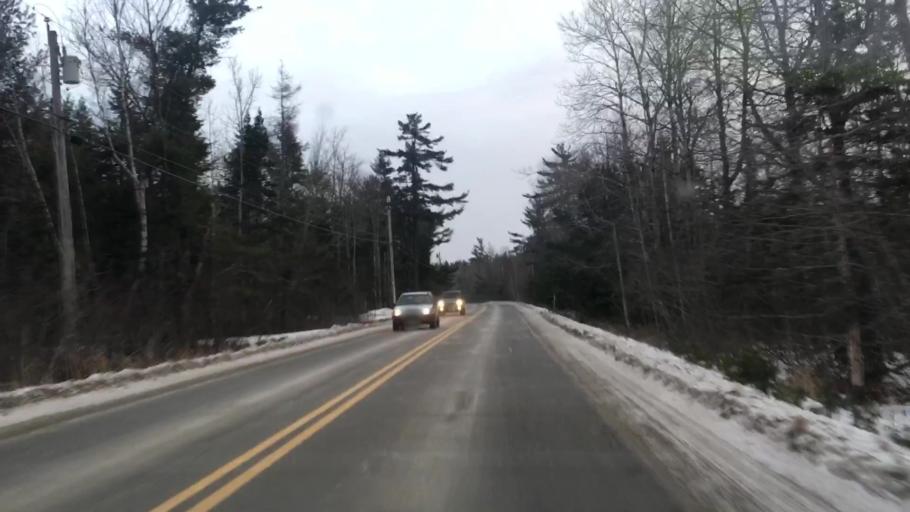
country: US
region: Maine
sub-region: Hancock County
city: Ellsworth
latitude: 44.6175
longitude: -68.3847
